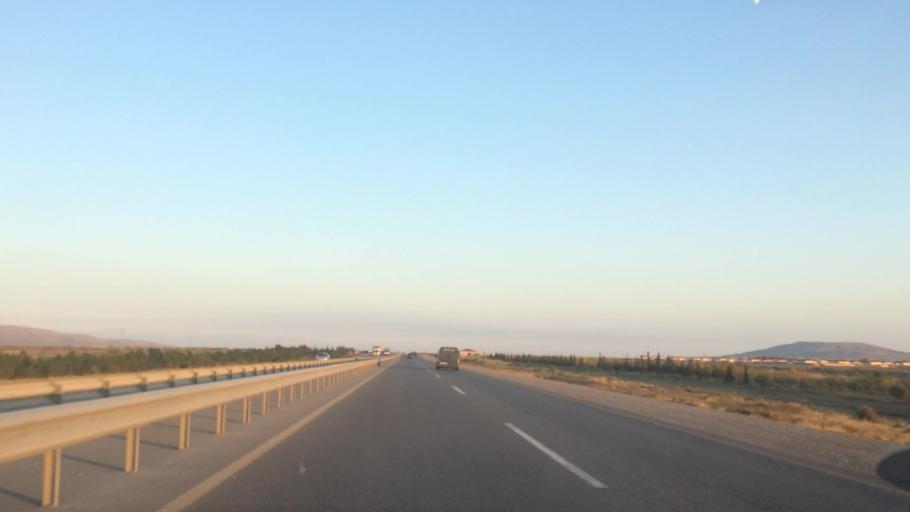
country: AZ
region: Baki
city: Qobustan
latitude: 39.9880
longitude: 49.2038
